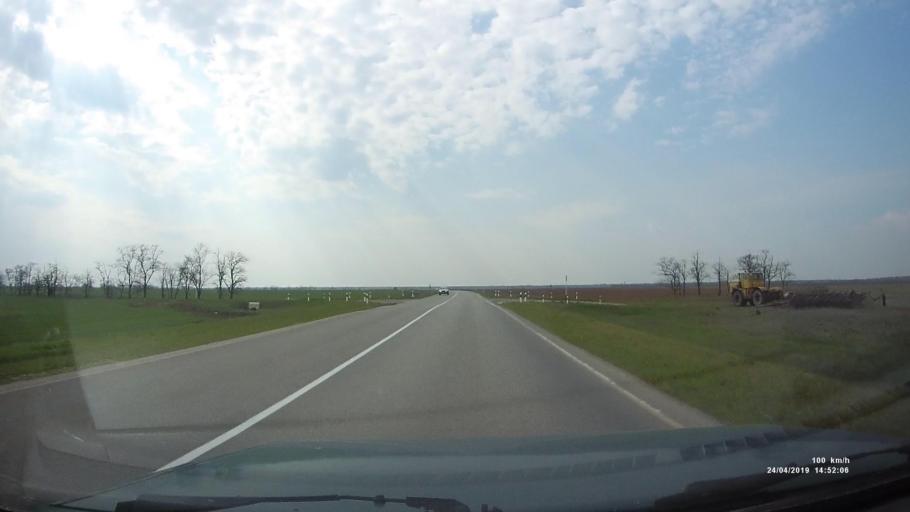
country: RU
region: Rostov
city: Remontnoye
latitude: 46.5294
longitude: 43.6877
